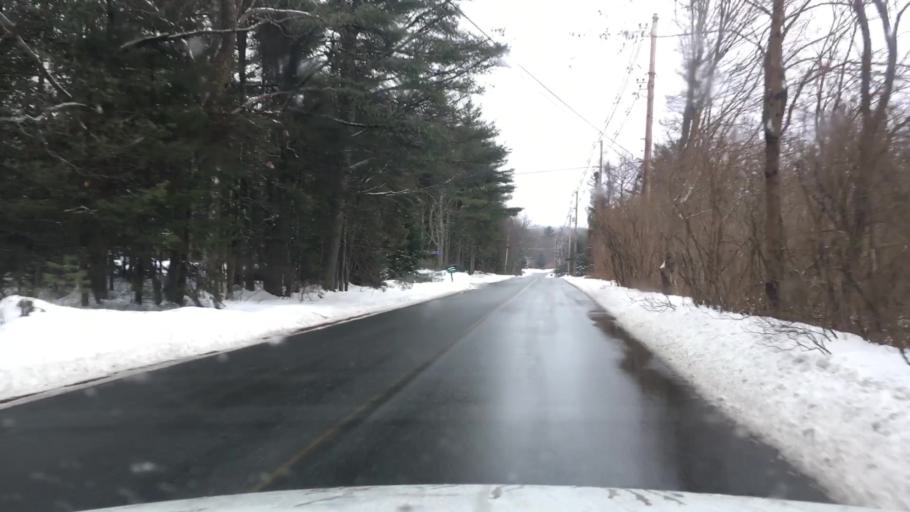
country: US
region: Maine
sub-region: Hancock County
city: Trenton
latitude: 44.4147
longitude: -68.3346
